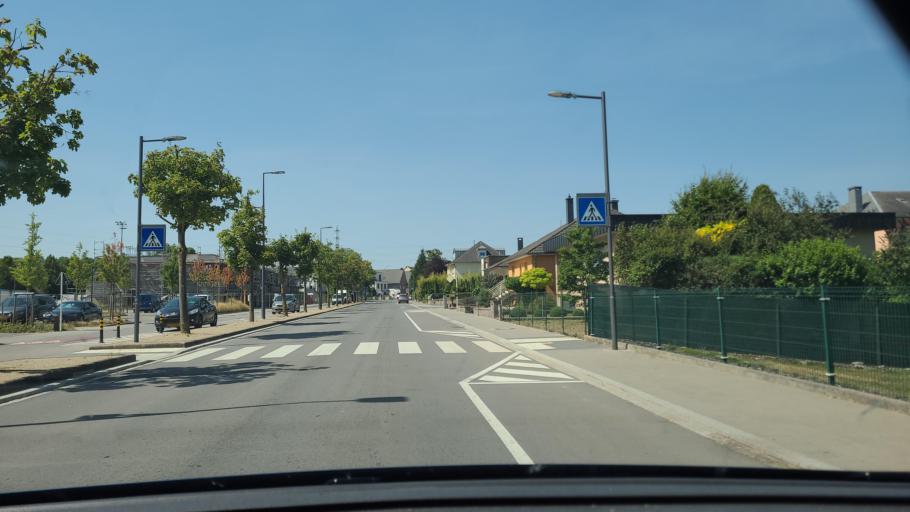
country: LU
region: Luxembourg
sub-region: Canton d'Esch-sur-Alzette
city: Sanem
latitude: 49.5458
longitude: 5.9240
